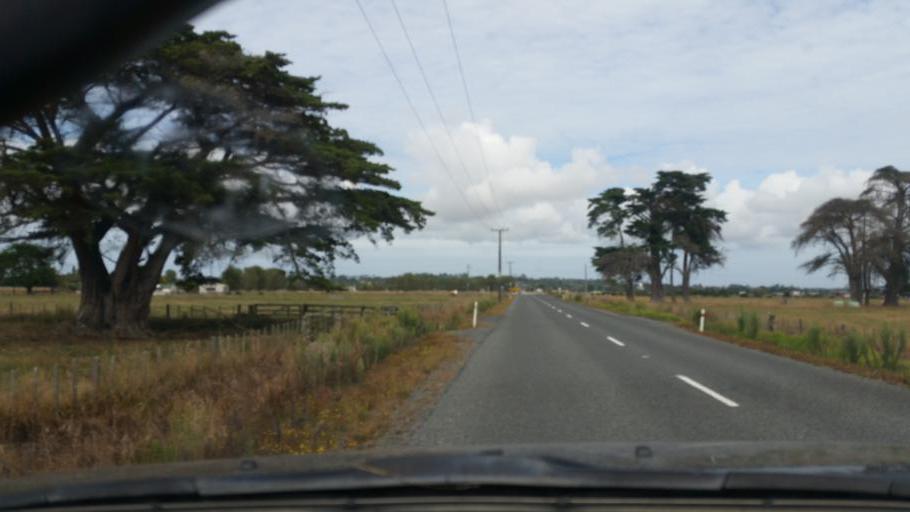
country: NZ
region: Northland
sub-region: Kaipara District
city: Dargaville
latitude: -35.9515
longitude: 173.8952
